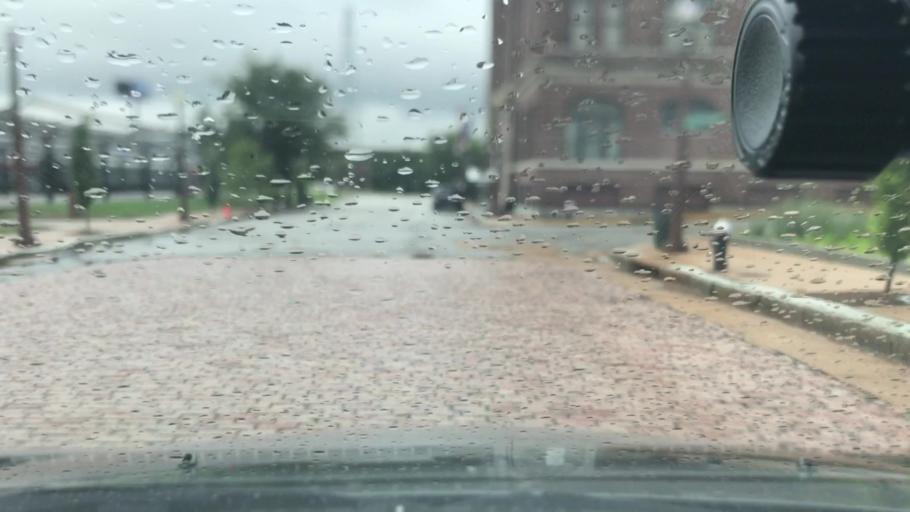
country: US
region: Missouri
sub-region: City of Saint Louis
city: St. Louis
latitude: 38.6284
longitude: -90.2097
